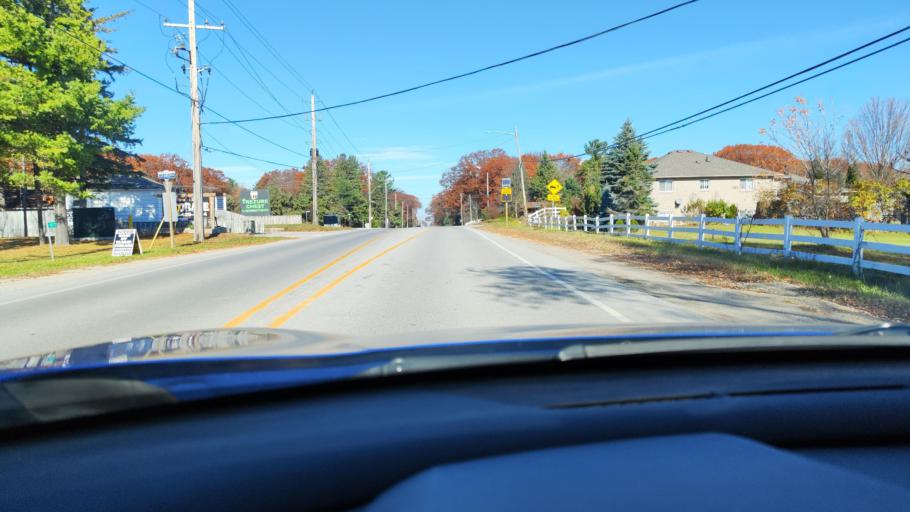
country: CA
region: Ontario
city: Wasaga Beach
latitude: 44.4630
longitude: -80.0734
